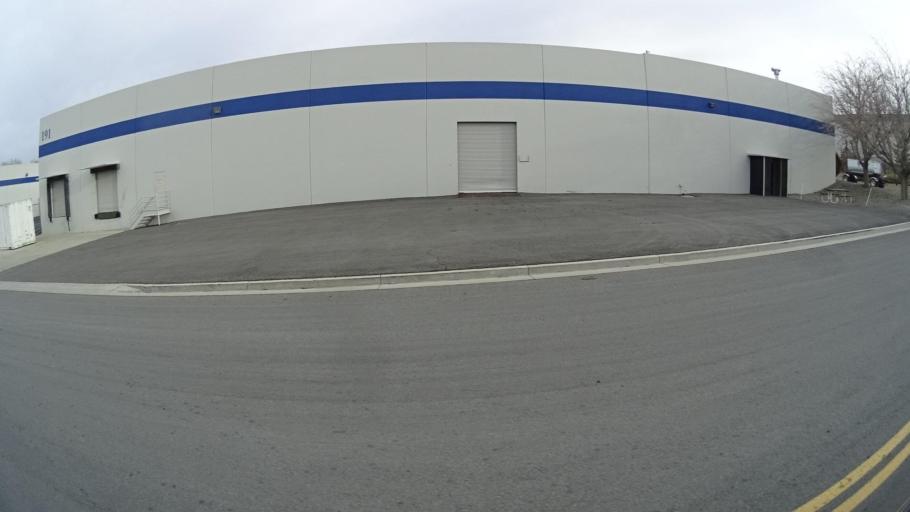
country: US
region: Nevada
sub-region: Washoe County
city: Reno
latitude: 39.5703
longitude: -119.8213
